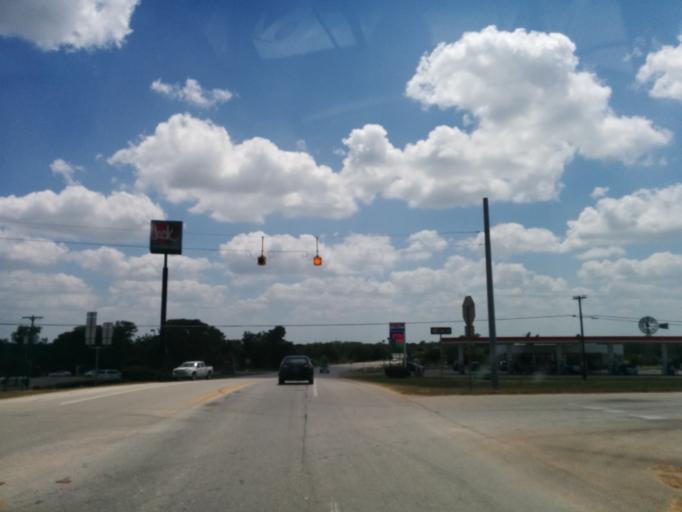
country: US
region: Texas
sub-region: Bastrop County
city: Wyldwood
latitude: 30.1124
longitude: -97.4153
